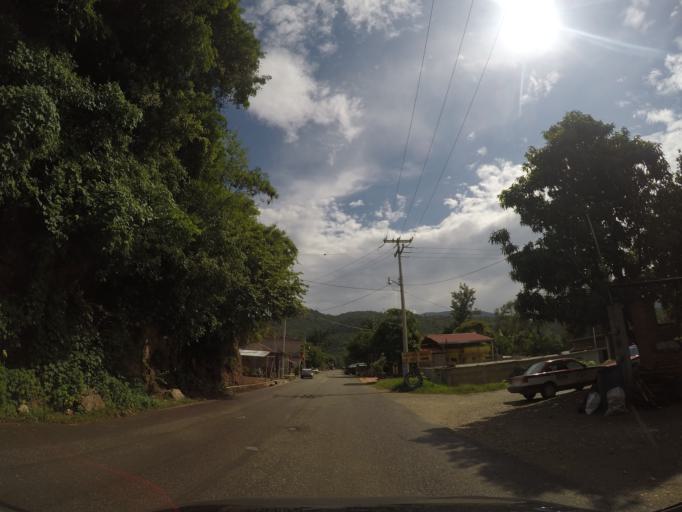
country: MX
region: Oaxaca
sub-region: San Jeronimo Coatlan
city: San Cristobal Honduras
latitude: 16.3566
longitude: -97.0942
